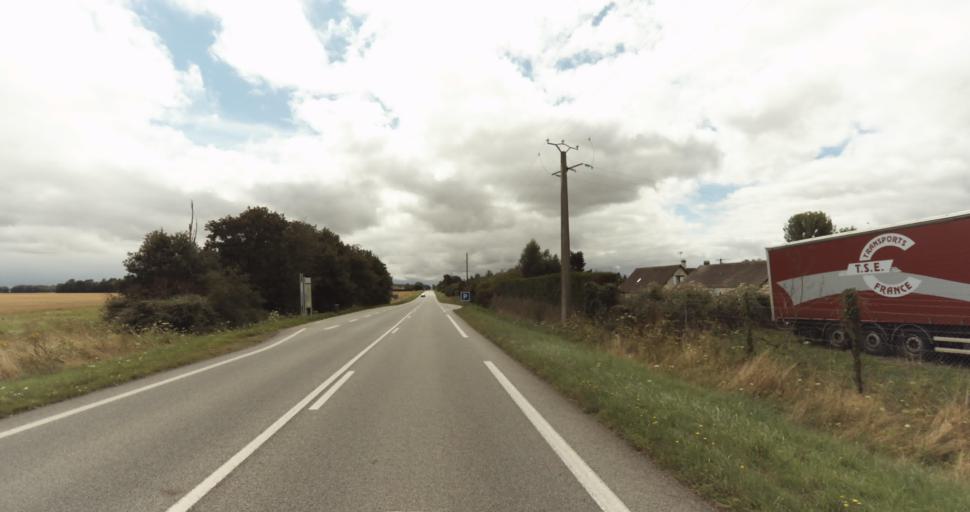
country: FR
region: Haute-Normandie
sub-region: Departement de l'Eure
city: Evreux
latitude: 48.9805
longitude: 1.1579
